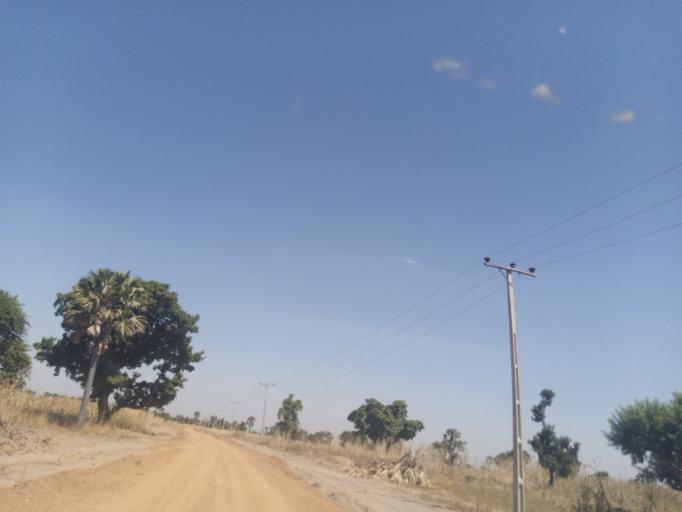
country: NG
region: Adamawa
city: Yola
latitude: 9.3001
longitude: 12.8884
